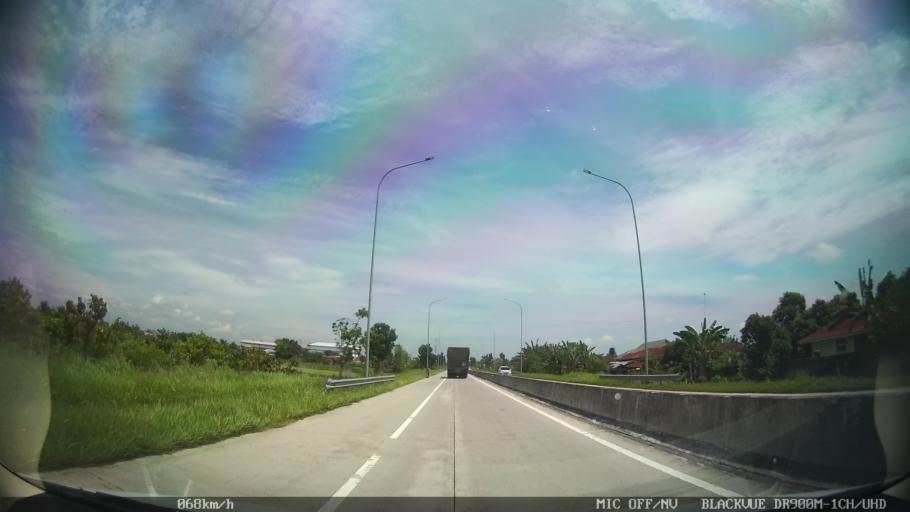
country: ID
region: North Sumatra
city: Perbaungan
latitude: 3.5503
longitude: 98.8883
